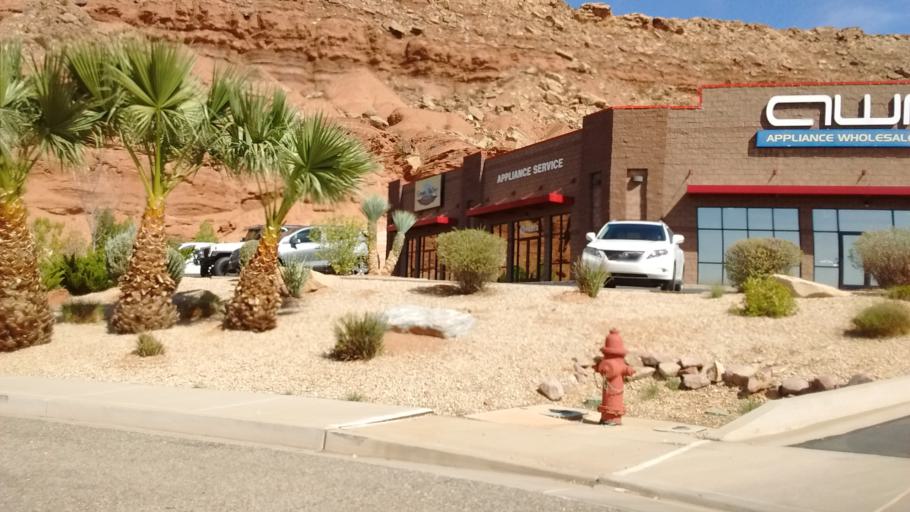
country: US
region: Utah
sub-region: Washington County
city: Saint George
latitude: 37.0638
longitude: -113.5807
